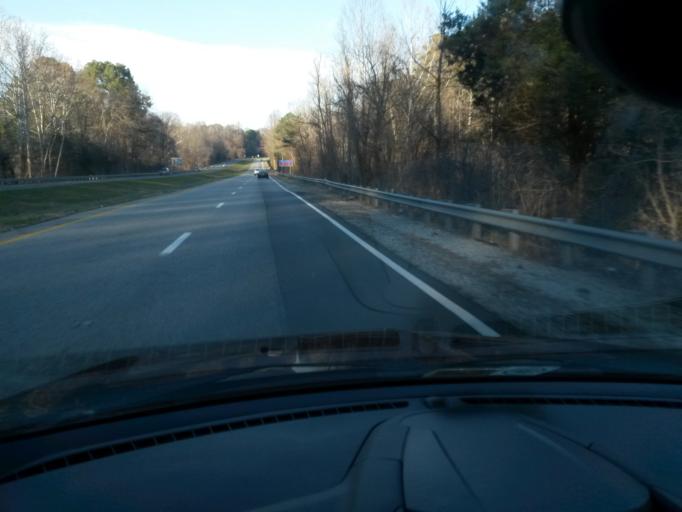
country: US
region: Virginia
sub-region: Amherst County
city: Amherst
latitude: 37.5711
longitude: -79.0528
